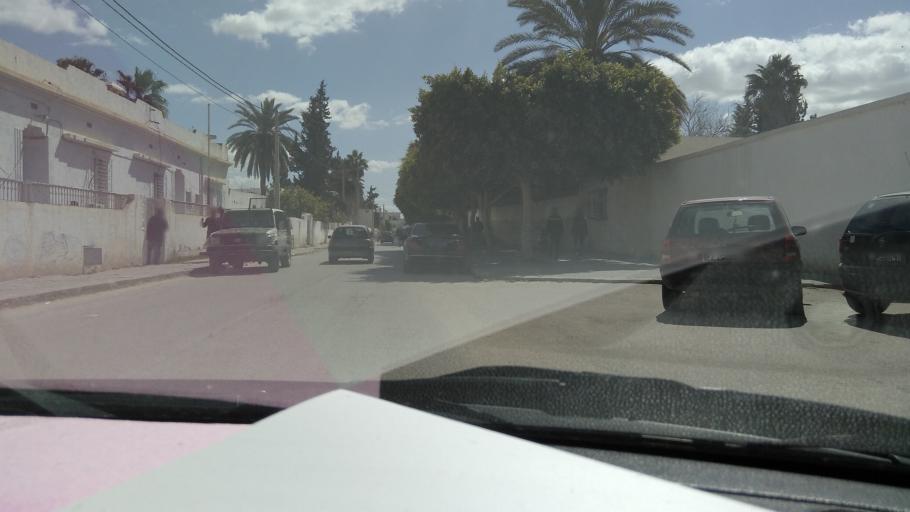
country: TN
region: Al Qayrawan
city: Kairouan
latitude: 35.6707
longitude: 10.1060
